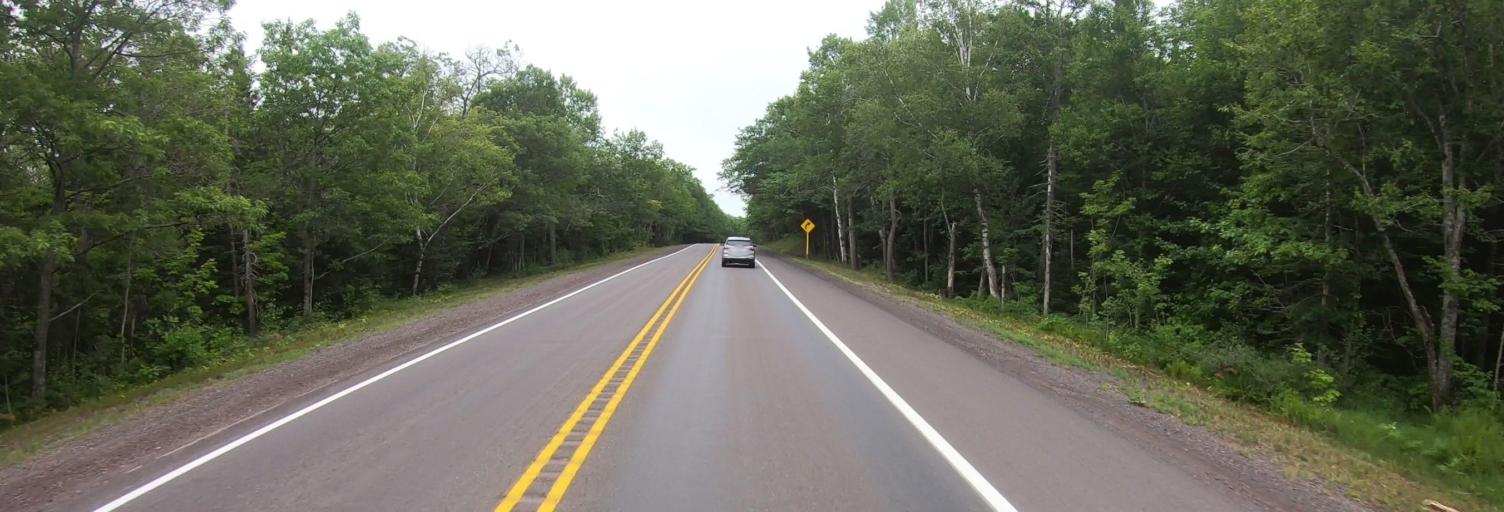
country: US
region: Michigan
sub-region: Keweenaw County
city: Eagle River
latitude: 47.3632
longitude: -88.3050
